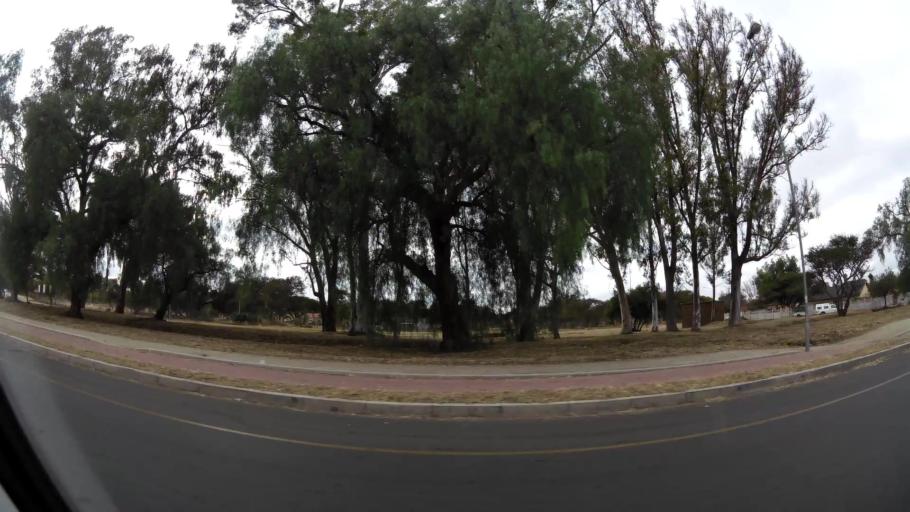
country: ZA
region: Limpopo
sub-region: Capricorn District Municipality
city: Polokwane
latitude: -23.9248
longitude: 29.4518
